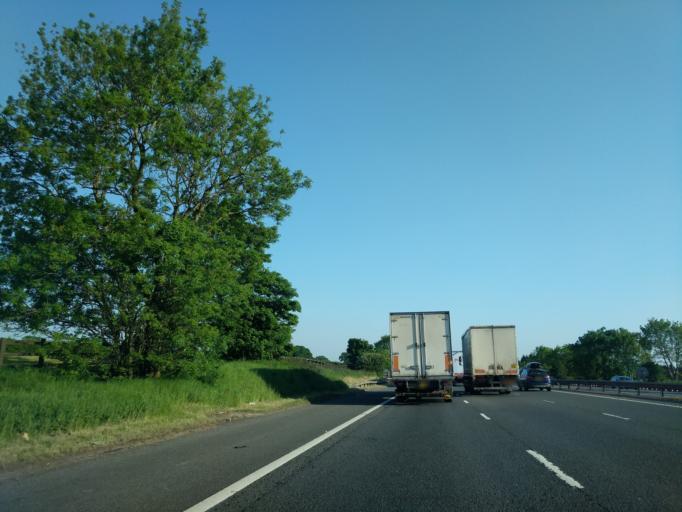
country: GB
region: England
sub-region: Staffordshire
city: Audley
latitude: 53.0595
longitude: -2.3315
